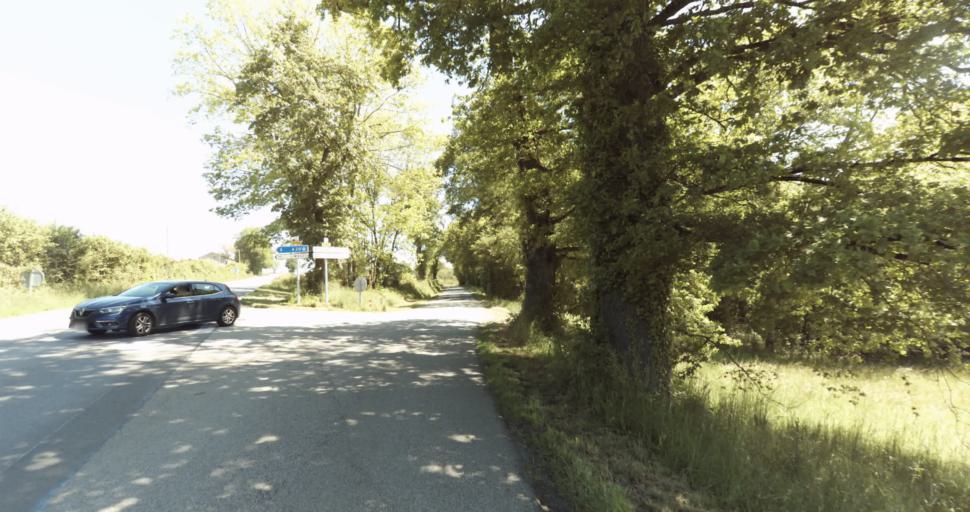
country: FR
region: Limousin
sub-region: Departement de la Haute-Vienne
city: Le Vigen
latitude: 45.7614
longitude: 1.2942
